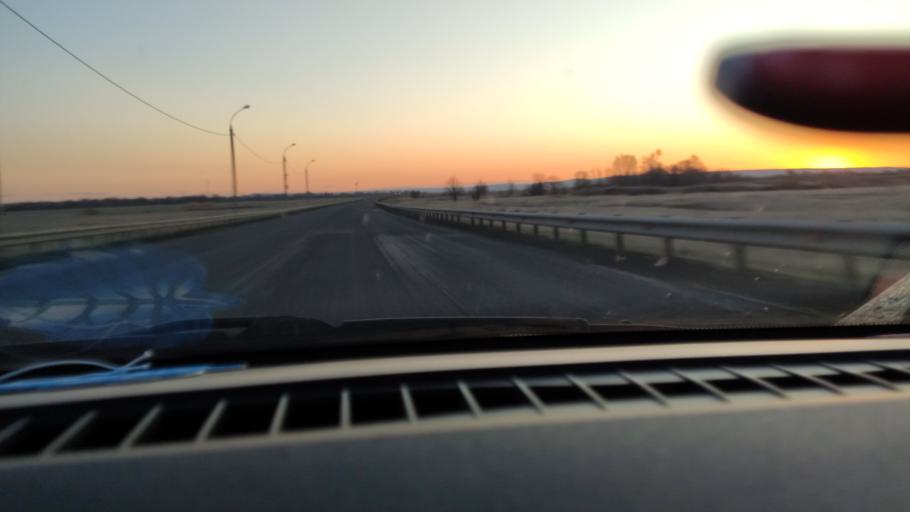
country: RU
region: Saratov
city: Yelshanka
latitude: 51.8055
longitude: 46.1939
